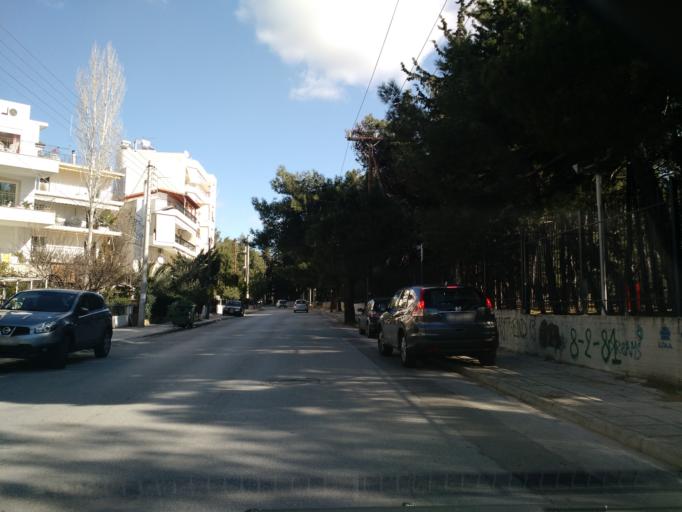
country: GR
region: Attica
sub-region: Nomarchia Athinas
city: Cholargos
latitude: 37.9982
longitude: 23.8149
